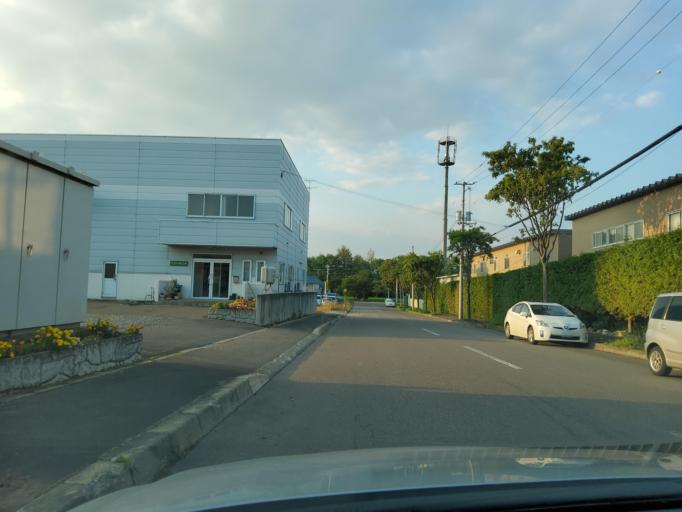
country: JP
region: Hokkaido
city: Obihiro
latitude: 42.9331
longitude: 143.1468
